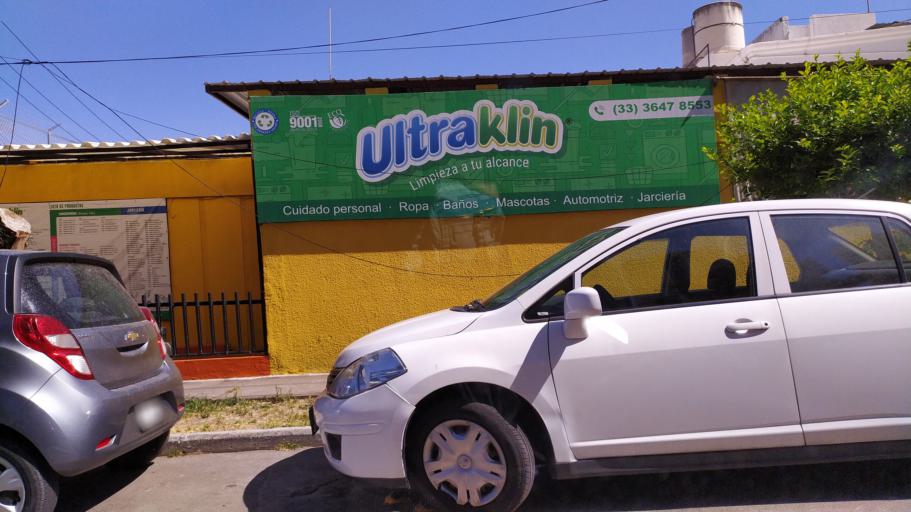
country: MX
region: Jalisco
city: Guadalajara
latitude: 20.6763
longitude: -103.4003
